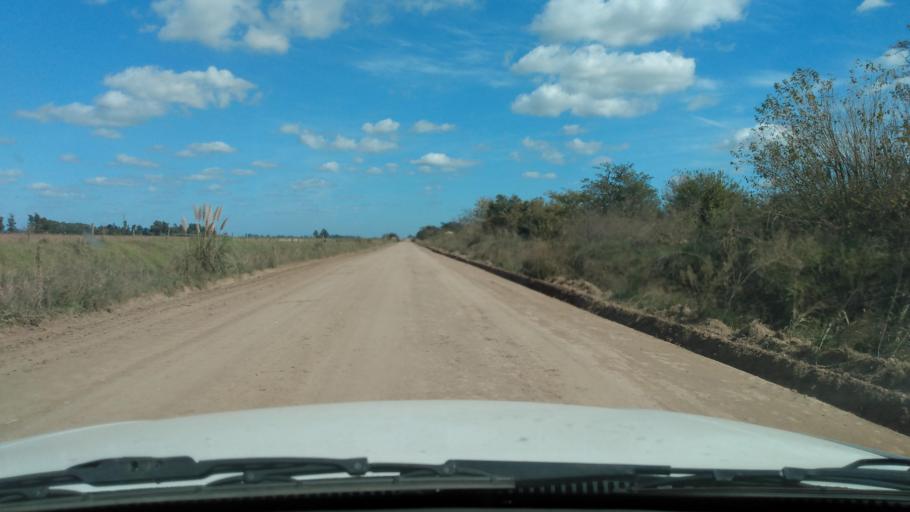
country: AR
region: Buenos Aires
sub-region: Partido de Navarro
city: Navarro
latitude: -35.0414
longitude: -59.4711
